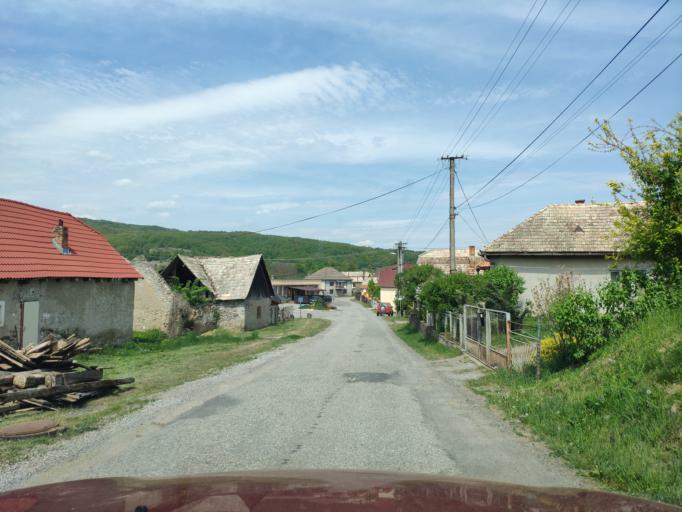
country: SK
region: Banskobystricky
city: Rimavska Sobota
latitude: 48.4804
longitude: 20.0719
